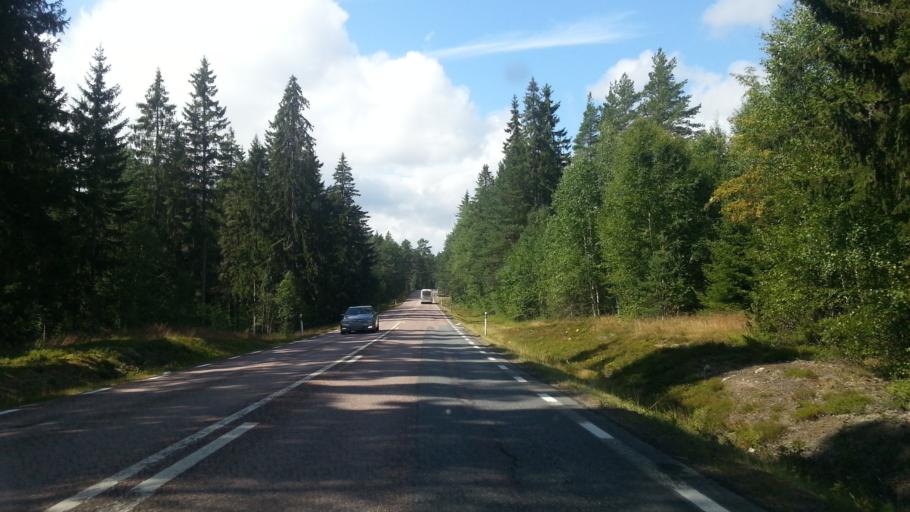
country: SE
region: Dalarna
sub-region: Faluns Kommun
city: Falun
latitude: 60.6126
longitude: 15.7389
